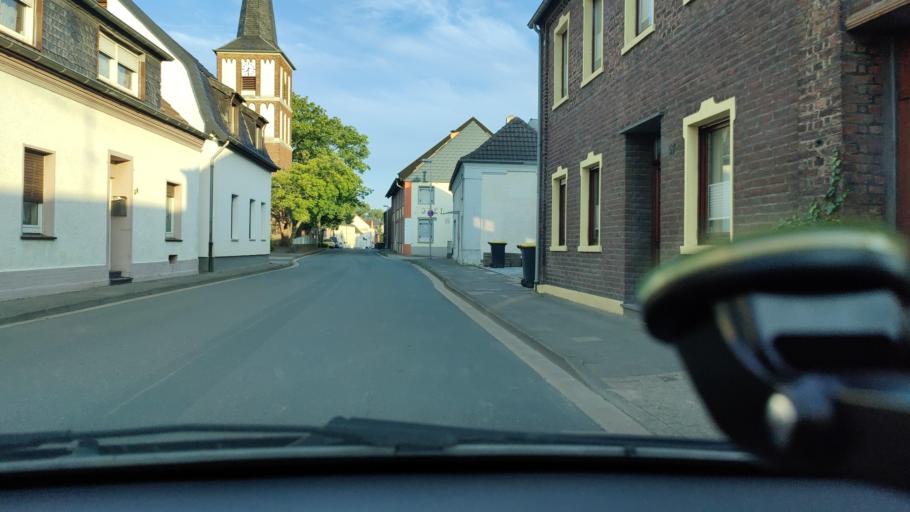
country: DE
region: North Rhine-Westphalia
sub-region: Regierungsbezirk Dusseldorf
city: Issum
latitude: 51.5102
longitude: 6.4699
